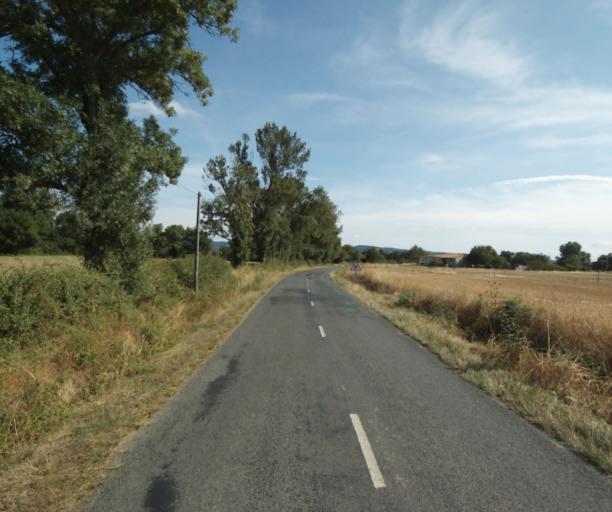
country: FR
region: Midi-Pyrenees
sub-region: Departement de la Haute-Garonne
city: Revel
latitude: 43.4804
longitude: 1.9894
